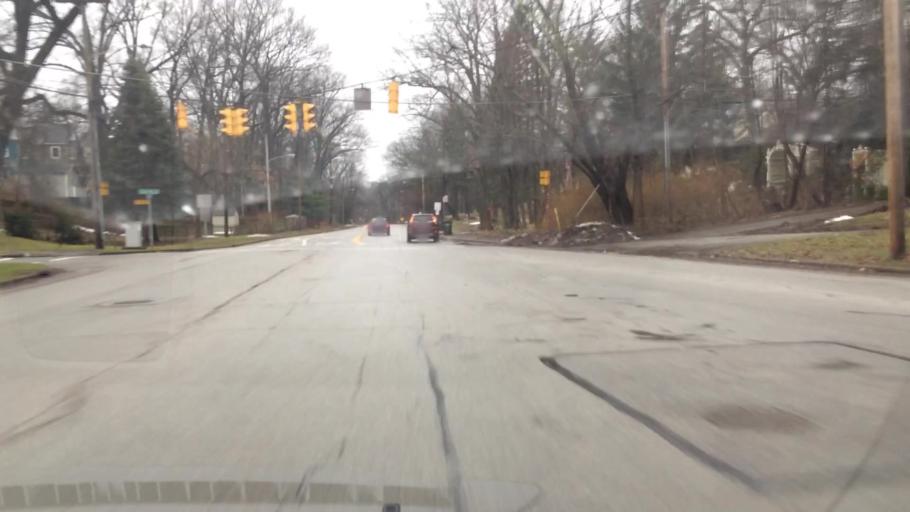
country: US
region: Ohio
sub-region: Summit County
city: Cuyahoga Falls
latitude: 41.1229
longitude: -81.4899
